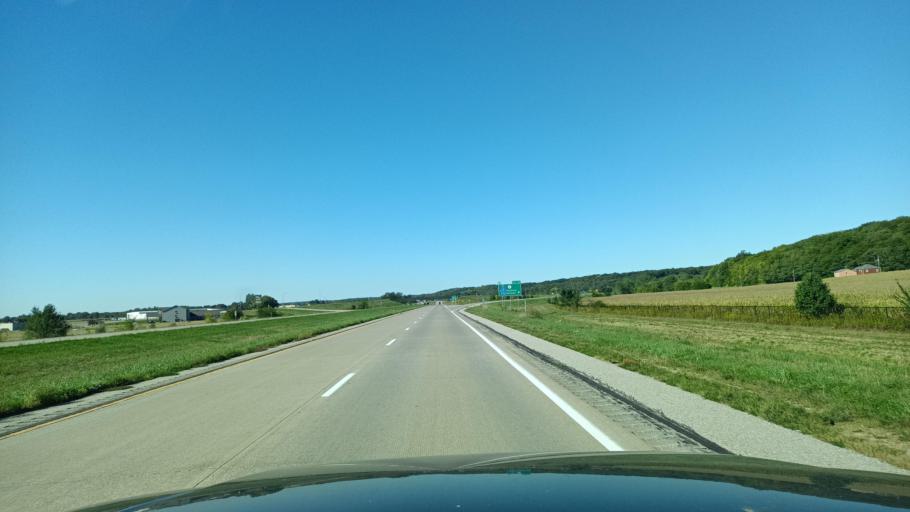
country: US
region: Iowa
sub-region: Lee County
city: Fort Madison
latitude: 40.6291
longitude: -91.3901
